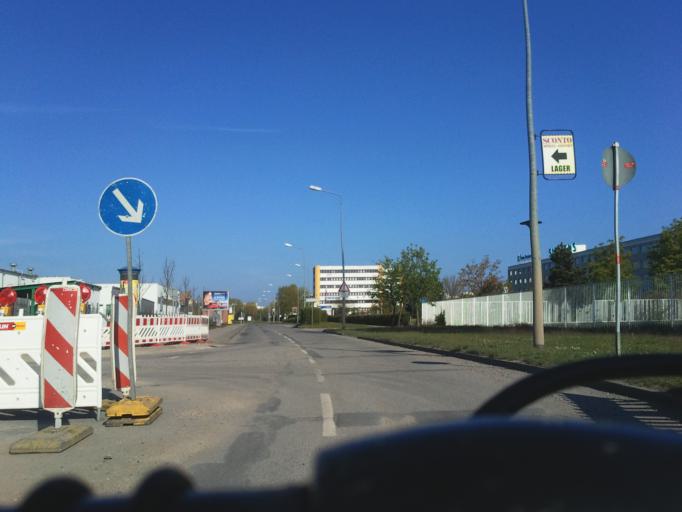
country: DE
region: Mecklenburg-Vorpommern
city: Warnemuende
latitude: 54.1254
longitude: 12.0809
